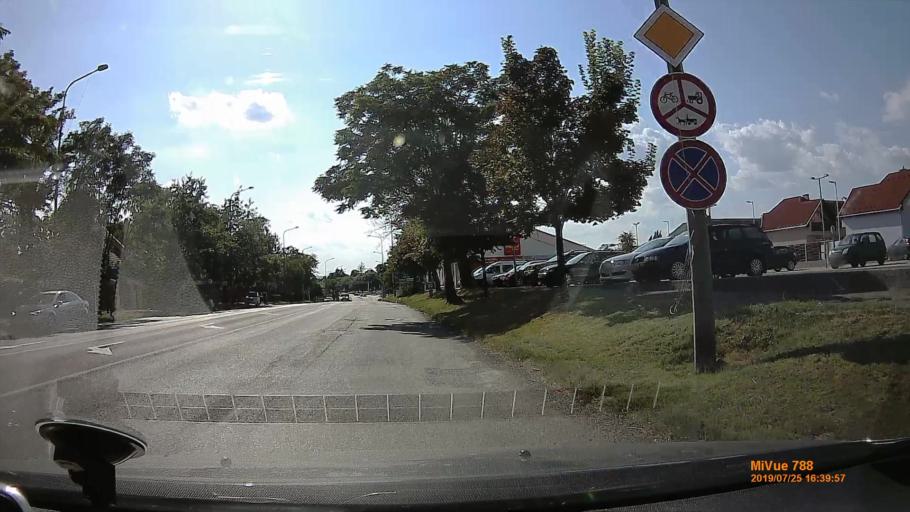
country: HU
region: Heves
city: Gyongyos
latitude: 47.7749
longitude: 19.9323
